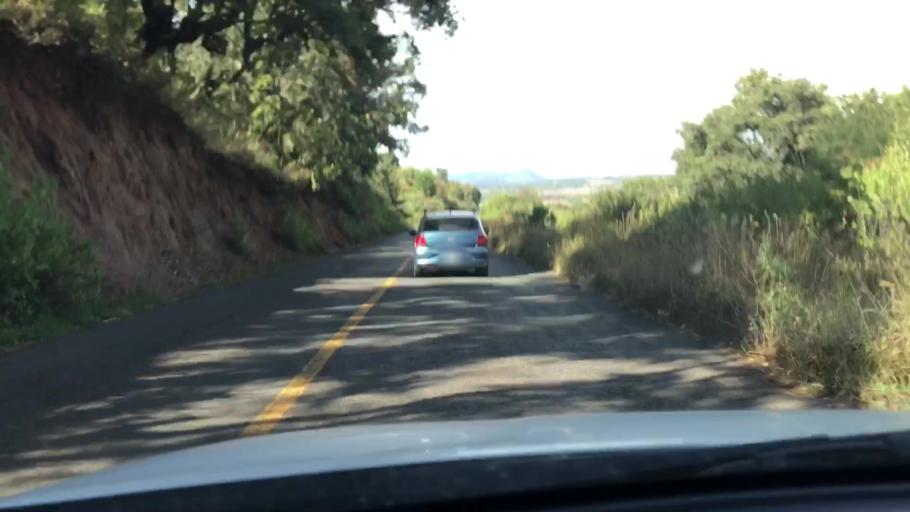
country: MX
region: Jalisco
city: Chiquilistlan
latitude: 20.1413
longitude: -103.7206
